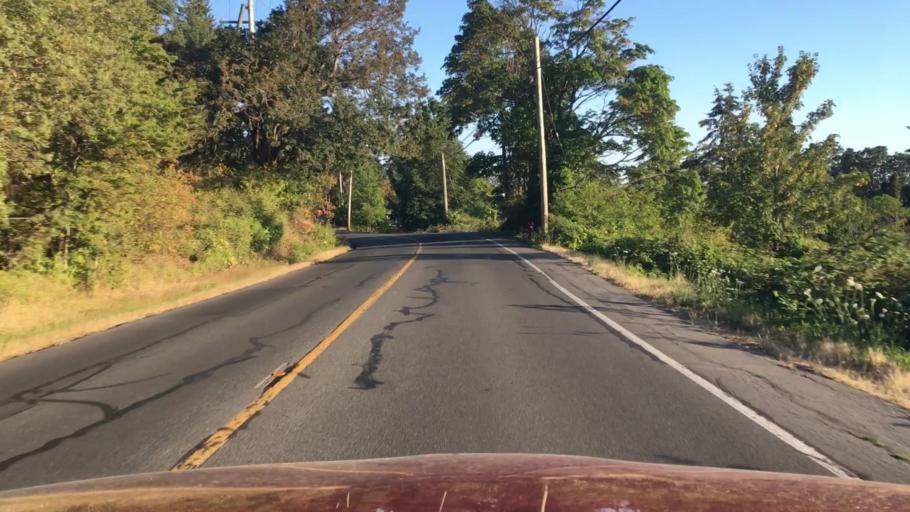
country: CA
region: British Columbia
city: Victoria
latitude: 48.4896
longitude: -123.3562
